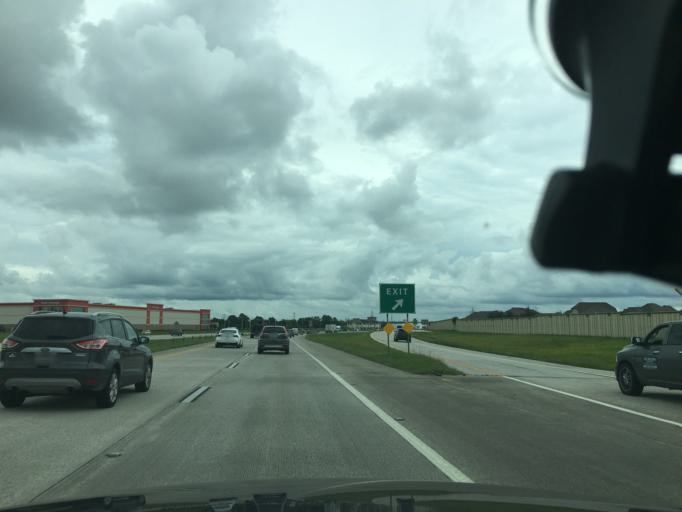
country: US
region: Texas
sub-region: Harris County
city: Tomball
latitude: 30.0823
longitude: -95.5374
